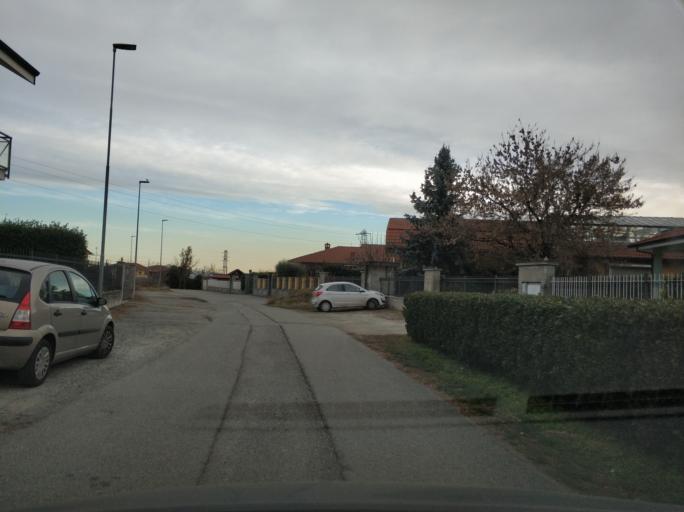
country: IT
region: Piedmont
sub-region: Provincia di Torino
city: San Maurizio
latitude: 45.2117
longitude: 7.6367
